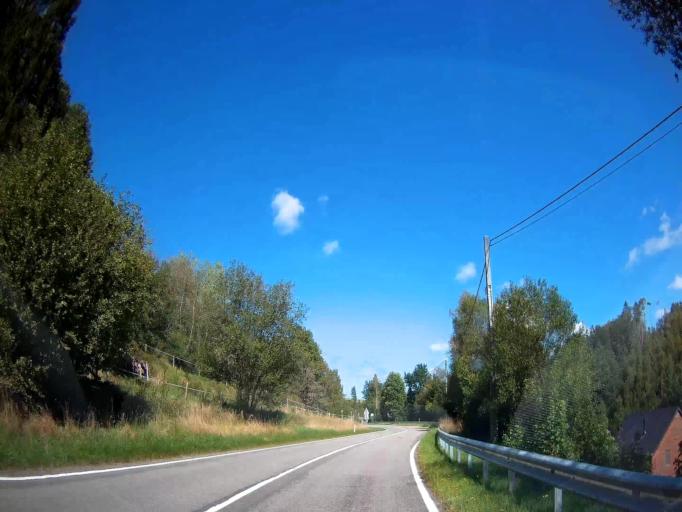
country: BE
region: Wallonia
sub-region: Province du Luxembourg
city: Bertogne
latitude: 50.1124
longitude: 5.6283
